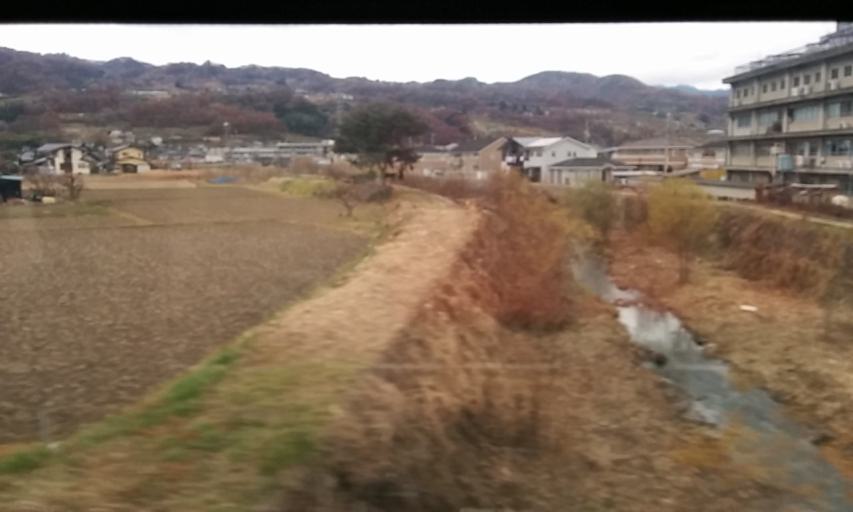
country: JP
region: Nagano
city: Nagano-shi
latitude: 36.5690
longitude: 138.1306
